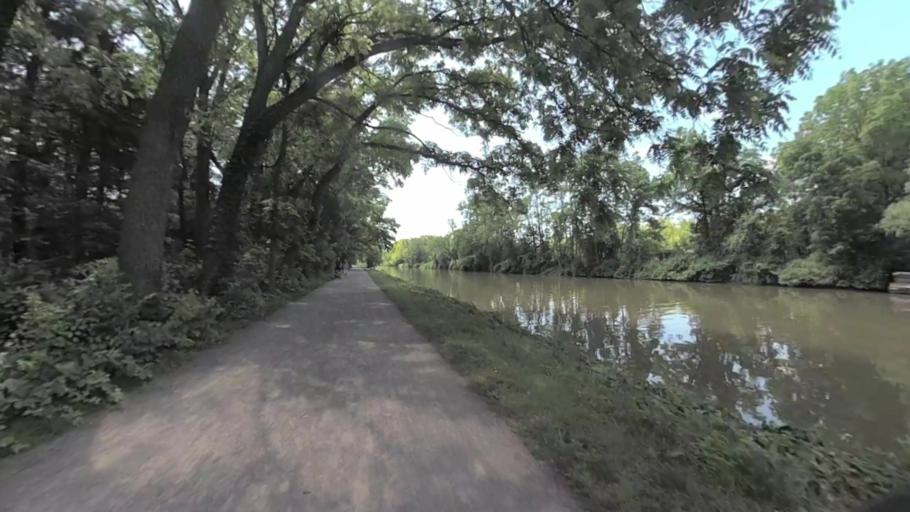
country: US
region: New York
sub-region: Monroe County
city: Pittsford
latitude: 43.0866
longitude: -77.5086
